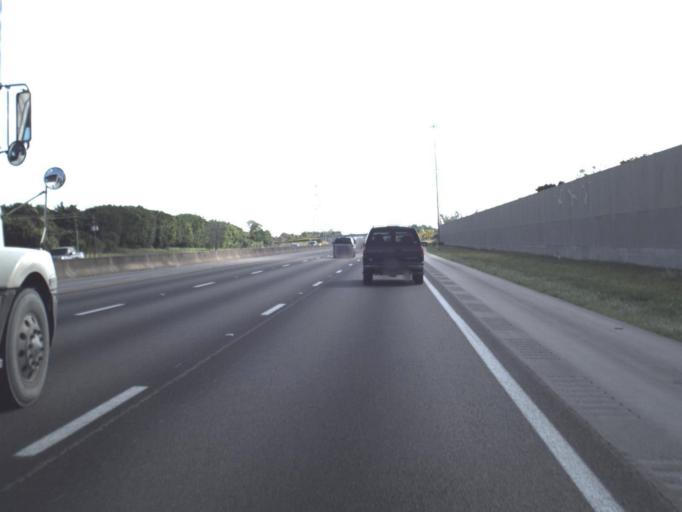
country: US
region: Florida
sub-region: Palm Beach County
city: Boca Del Mar
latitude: 26.3817
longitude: -80.1711
